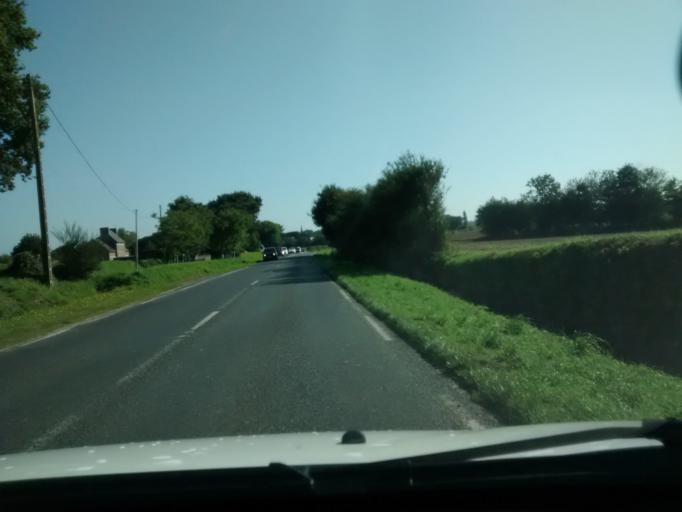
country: FR
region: Brittany
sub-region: Departement des Cotes-d'Armor
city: La Roche-Derrien
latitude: 48.7718
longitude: -3.2607
